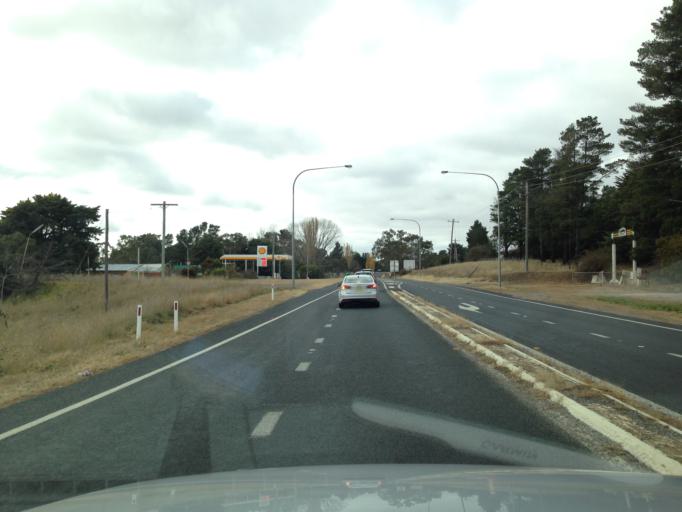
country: AU
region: New South Wales
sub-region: Cooma-Monaro
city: Cooma
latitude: -36.2468
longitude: 149.0519
